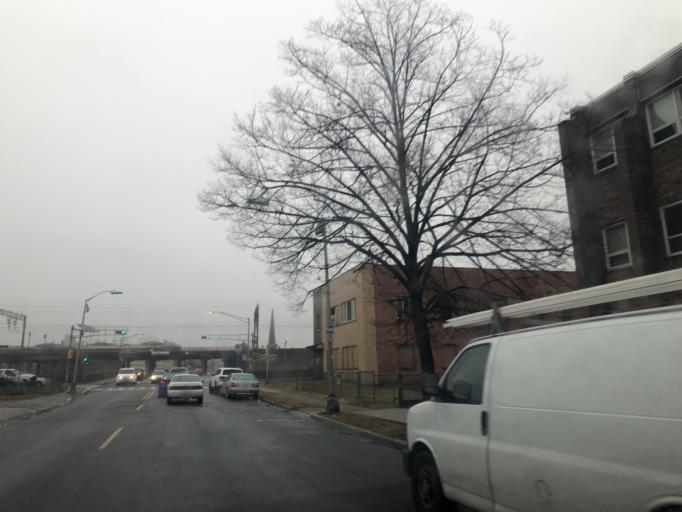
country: US
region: New Jersey
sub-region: Essex County
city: East Orange
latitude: 40.7637
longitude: -74.2189
